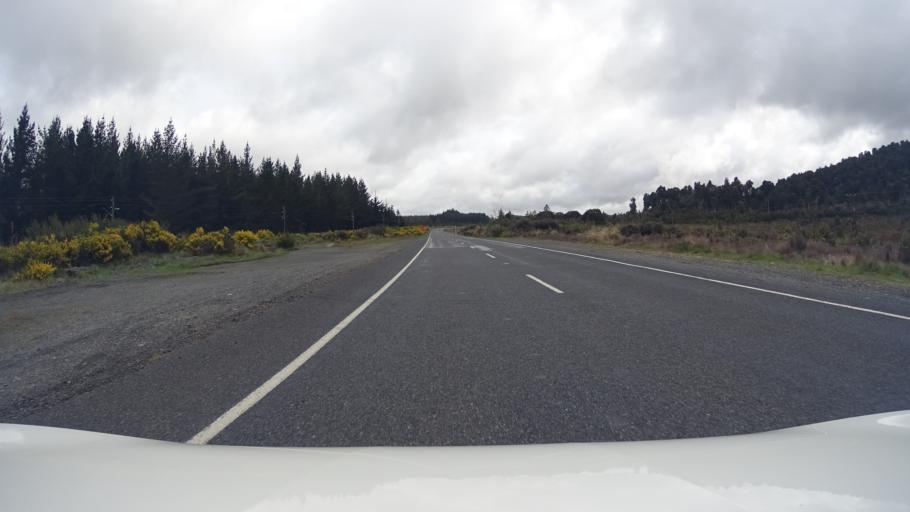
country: NZ
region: Manawatu-Wanganui
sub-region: Ruapehu District
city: Waiouru
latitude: -39.2203
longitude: 175.4008
